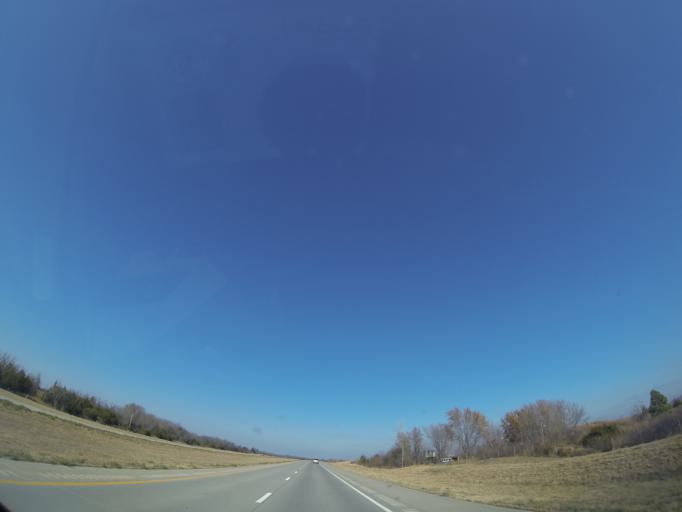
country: US
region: Kansas
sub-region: Reno County
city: Hutchinson
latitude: 38.1294
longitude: -97.8754
